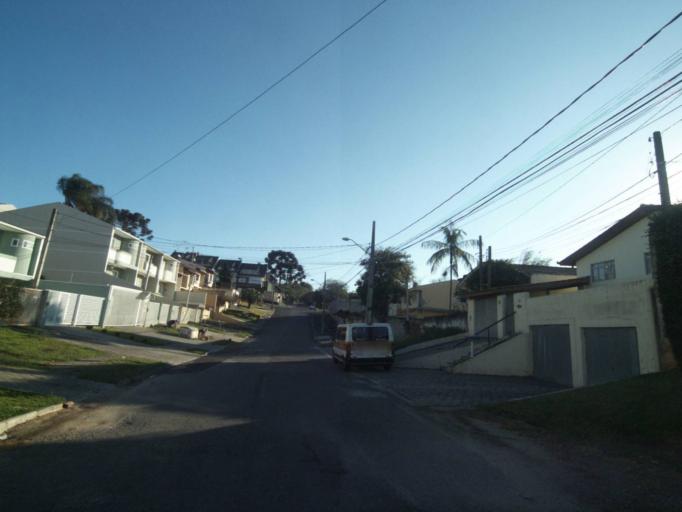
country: BR
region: Parana
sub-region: Curitiba
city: Curitiba
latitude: -25.3867
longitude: -49.2557
